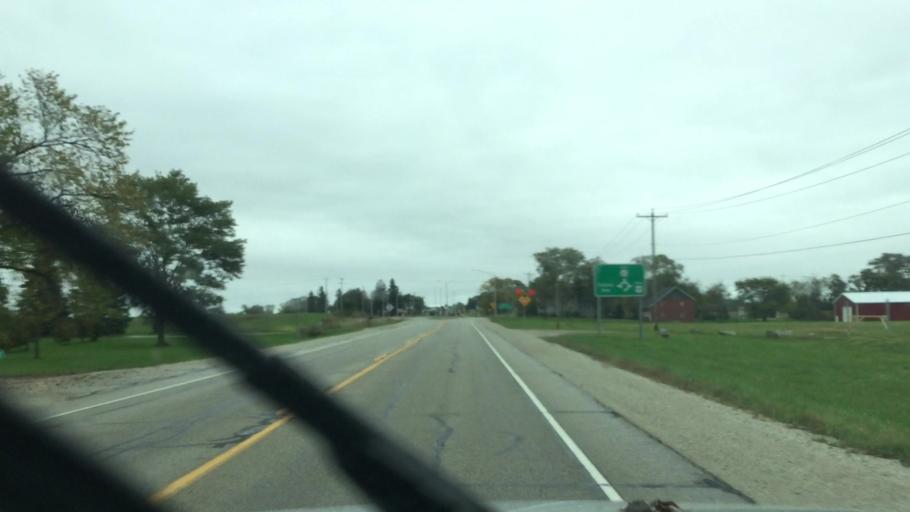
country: US
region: Wisconsin
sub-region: Racine County
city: Union Grove
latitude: 42.7422
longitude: -88.0565
